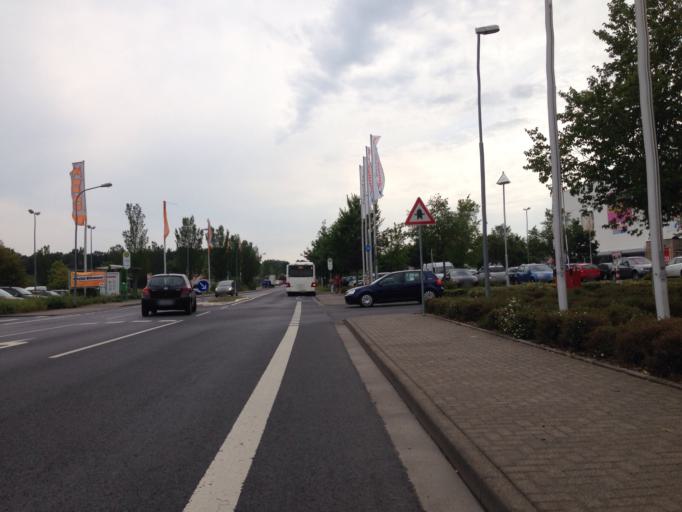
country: DE
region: Hesse
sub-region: Regierungsbezirk Giessen
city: Giessen
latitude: 50.5697
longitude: 8.6891
